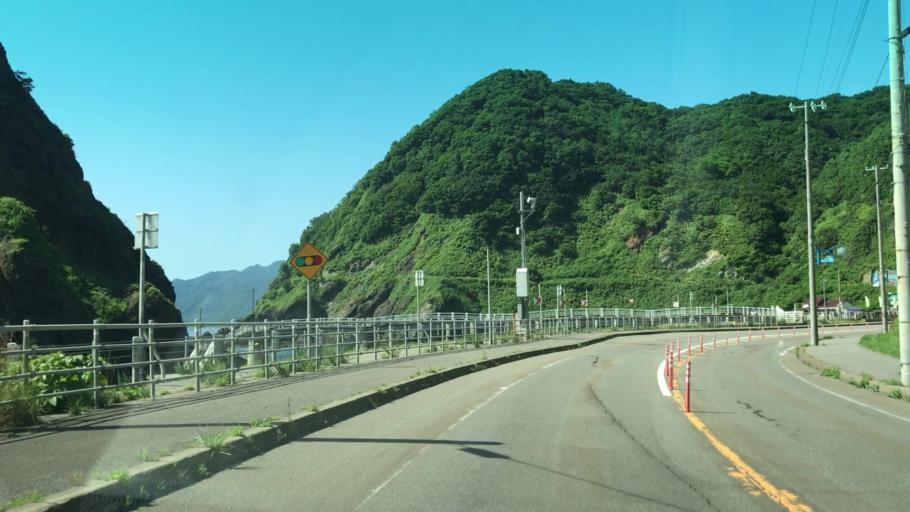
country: JP
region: Hokkaido
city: Iwanai
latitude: 43.1111
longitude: 140.4503
